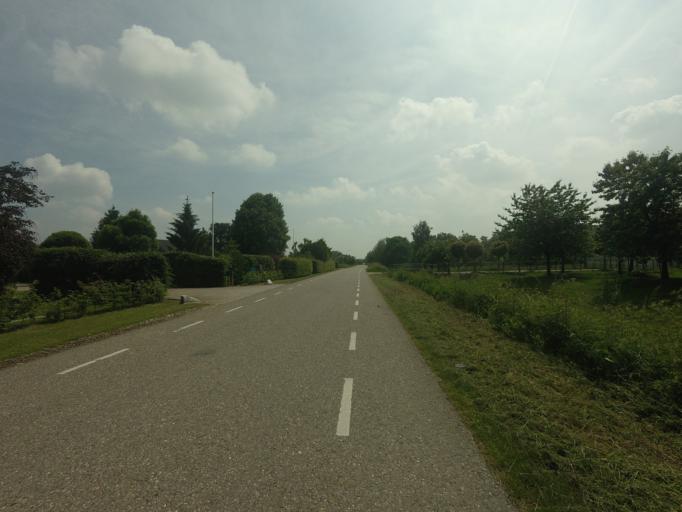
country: NL
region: Utrecht
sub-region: Gemeente Houten
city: Houten
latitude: 51.9981
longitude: 5.1460
